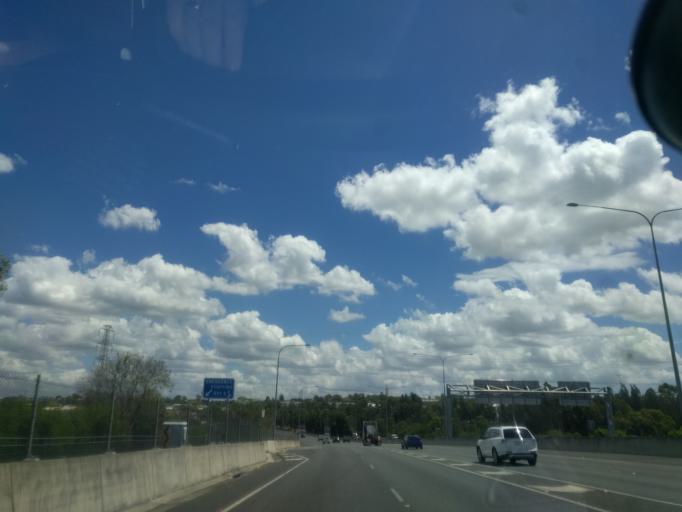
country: AU
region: Queensland
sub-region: Brisbane
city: Wacol
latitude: -27.5695
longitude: 152.9437
